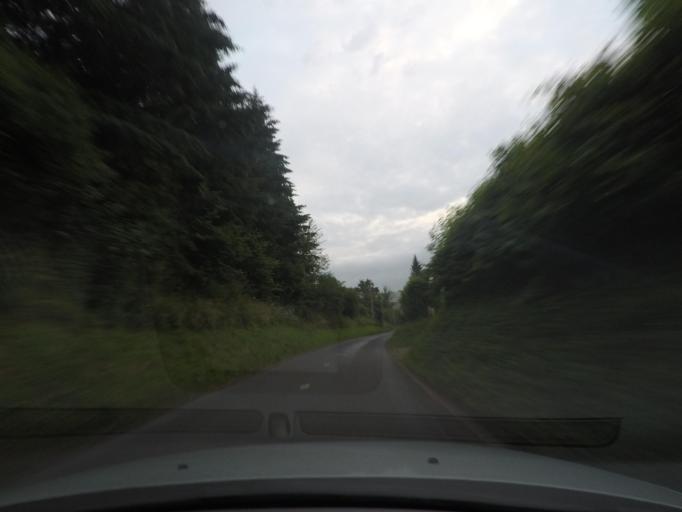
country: FR
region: Haute-Normandie
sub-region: Departement de la Seine-Maritime
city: Fontaine-le-Bourg
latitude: 49.5572
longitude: 1.1267
